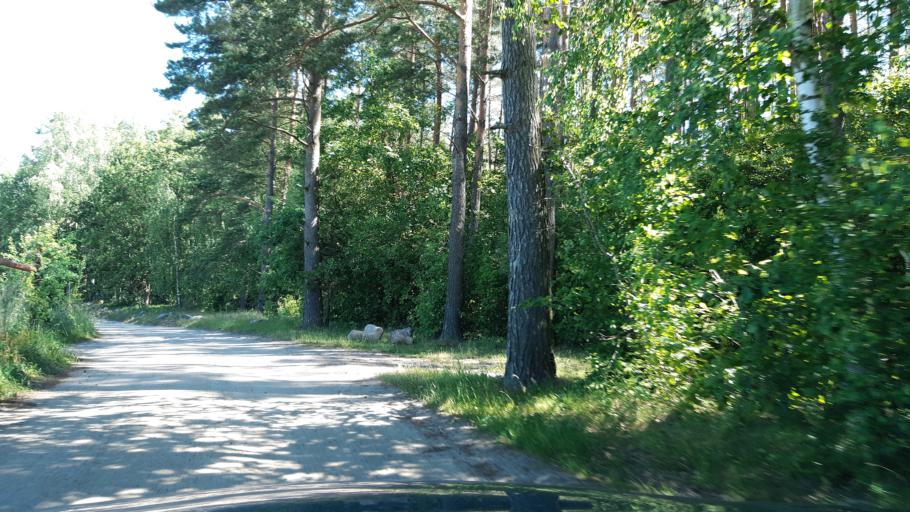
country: PL
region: Warmian-Masurian Voivodeship
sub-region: Powiat piski
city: Ruciane-Nida
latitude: 53.7105
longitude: 21.4887
